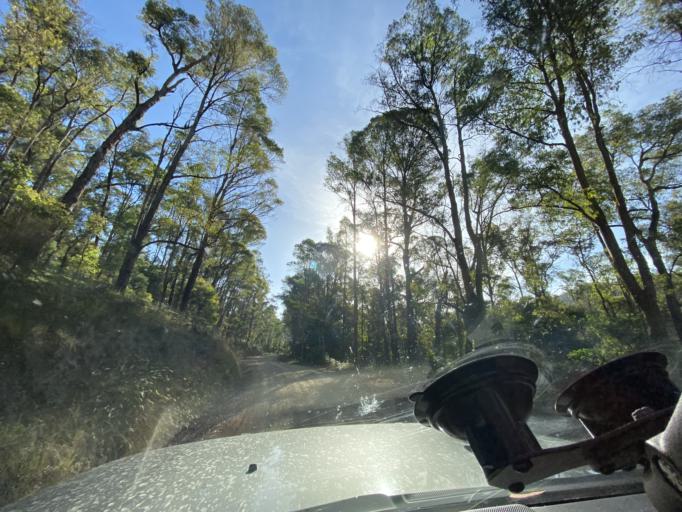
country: AU
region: Victoria
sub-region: Mansfield
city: Mansfield
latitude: -37.5189
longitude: 146.0638
